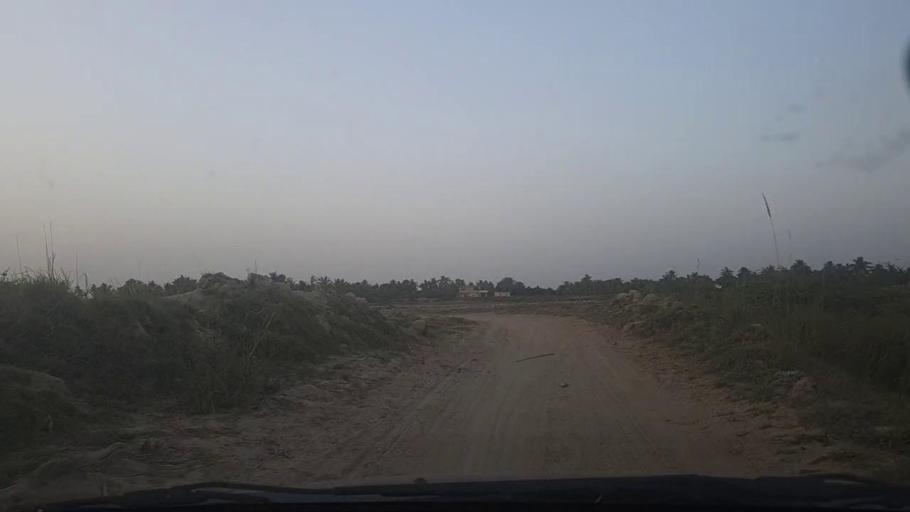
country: PK
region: Sindh
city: Mirpur Sakro
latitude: 24.3790
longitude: 67.6570
